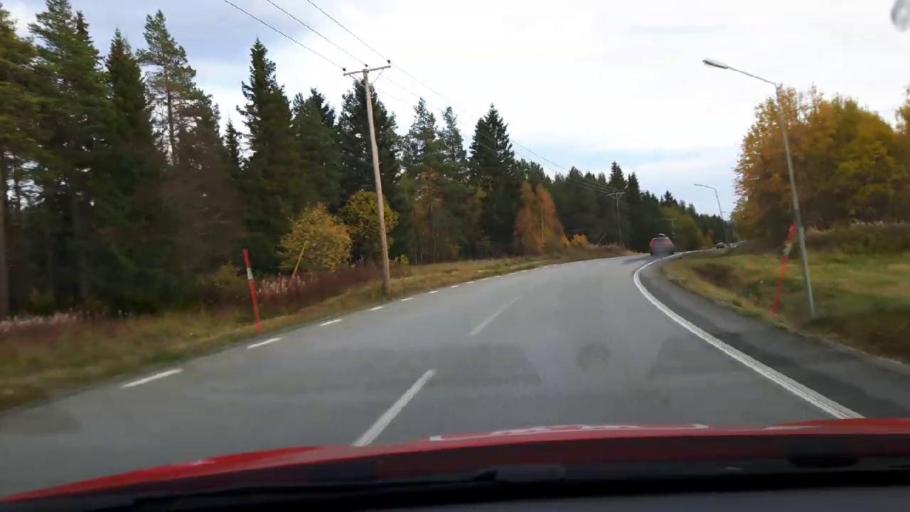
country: SE
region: Jaemtland
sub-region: Krokoms Kommun
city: Krokom
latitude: 63.3365
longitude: 14.5990
